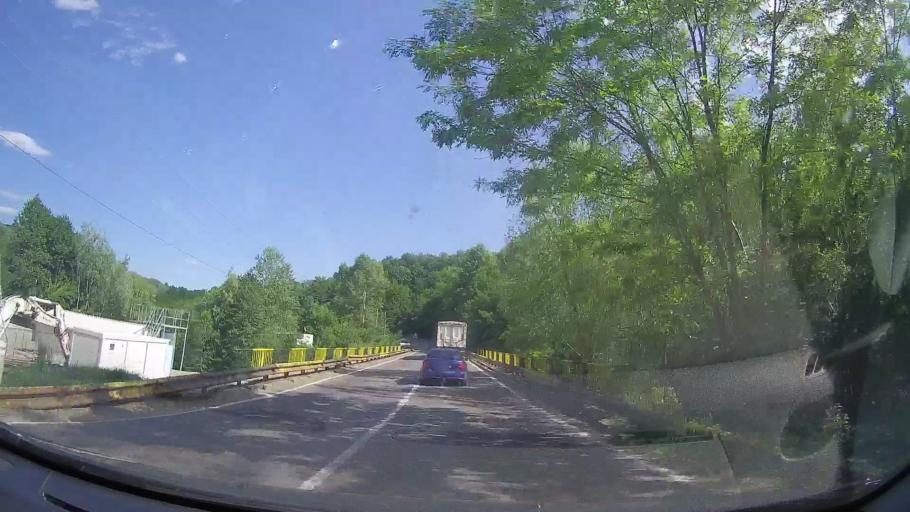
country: RO
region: Prahova
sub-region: Comuna Izvoarele
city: Homoraciu
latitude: 45.2737
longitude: 26.0131
